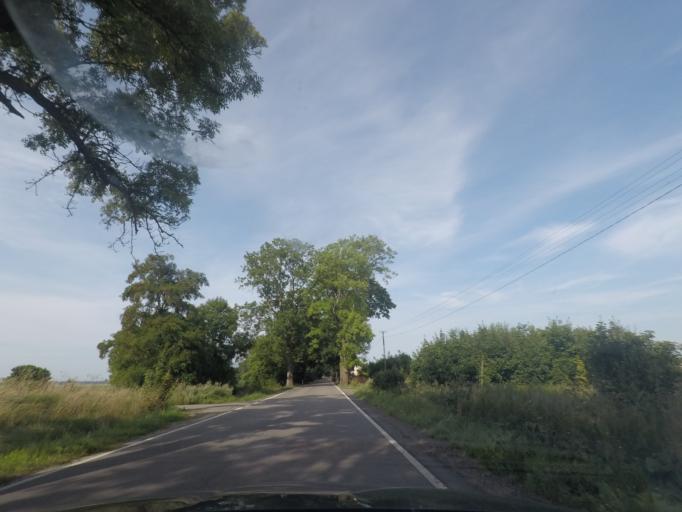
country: PL
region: Pomeranian Voivodeship
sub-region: Powiat leborski
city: Leba
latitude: 54.6403
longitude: 17.5343
